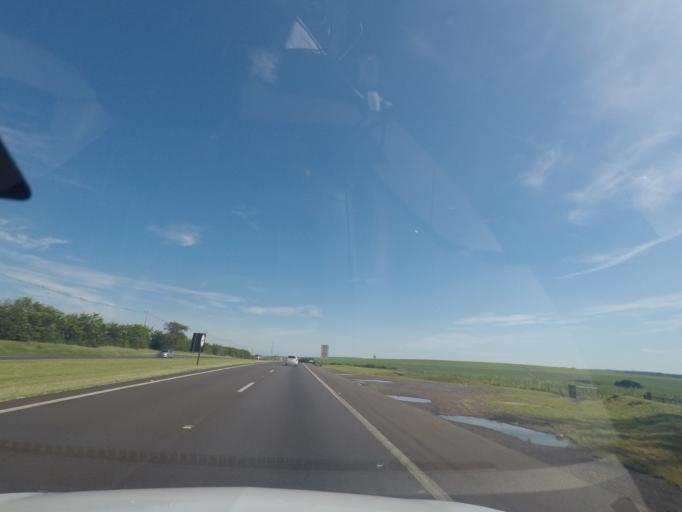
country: BR
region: Sao Paulo
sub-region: Itirapina
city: Itirapina
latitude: -22.2086
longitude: -47.7696
